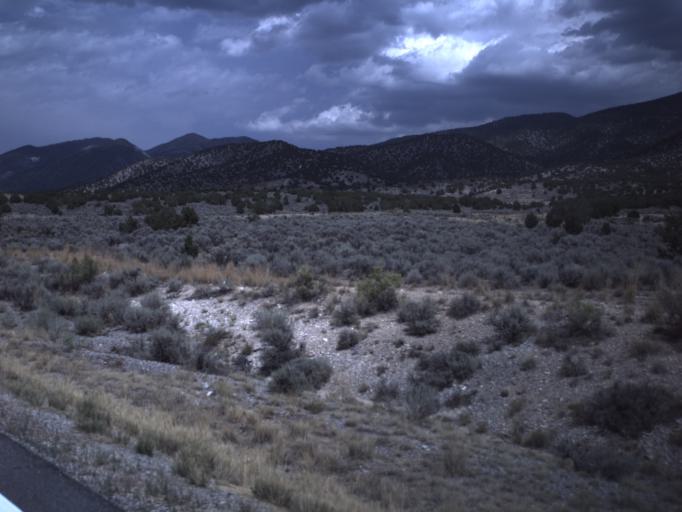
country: US
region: Utah
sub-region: Tooele County
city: Tooele
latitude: 40.3088
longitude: -112.2804
